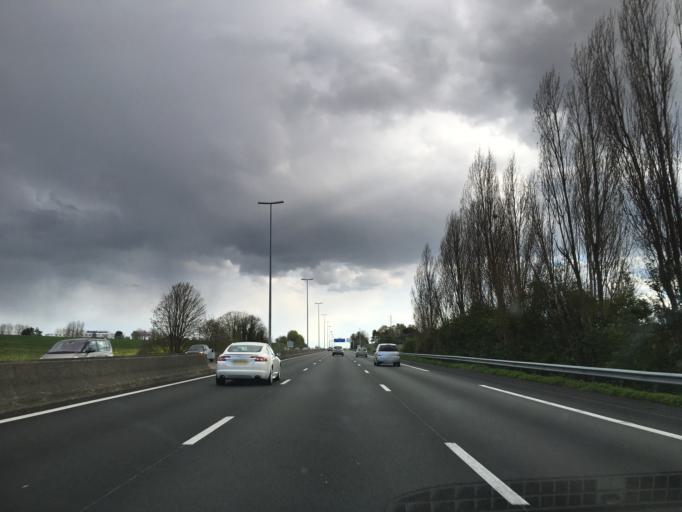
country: FR
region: Ile-de-France
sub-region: Departement du Val-d'Oise
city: Survilliers
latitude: 49.0950
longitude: 2.5501
